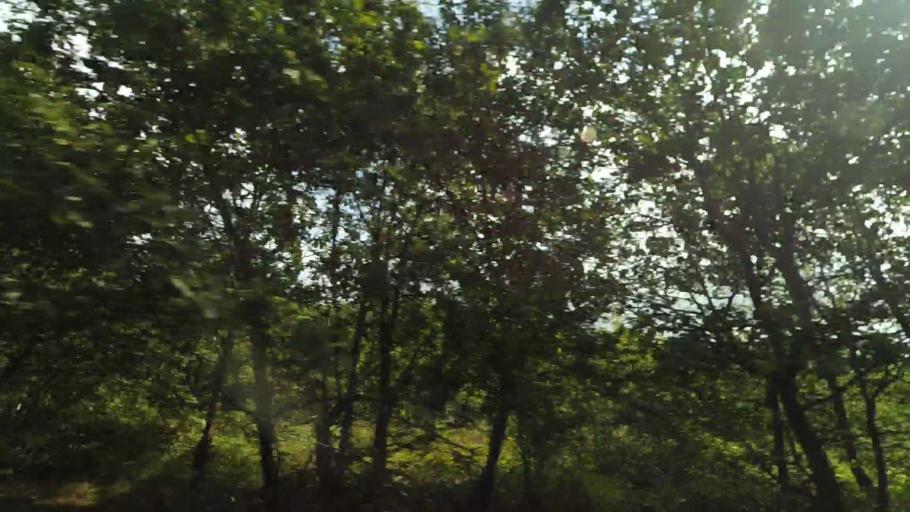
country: DK
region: Central Jutland
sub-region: Syddjurs Kommune
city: Ryomgard
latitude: 56.4575
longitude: 10.5428
